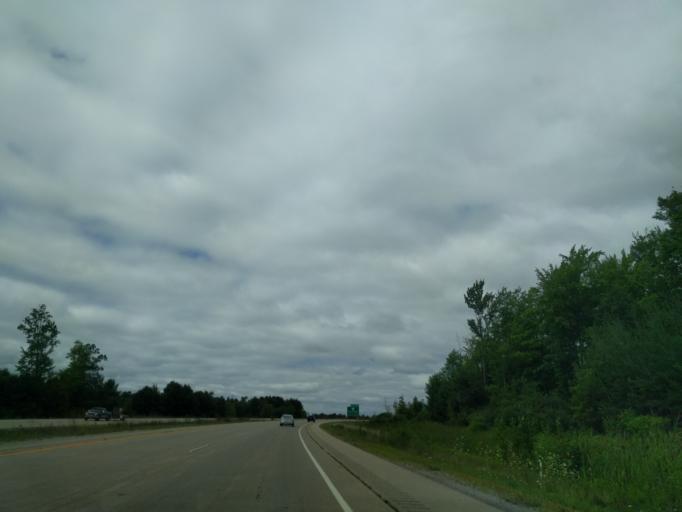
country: US
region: Wisconsin
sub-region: Marinette County
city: Peshtigo
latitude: 45.0396
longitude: -87.7487
